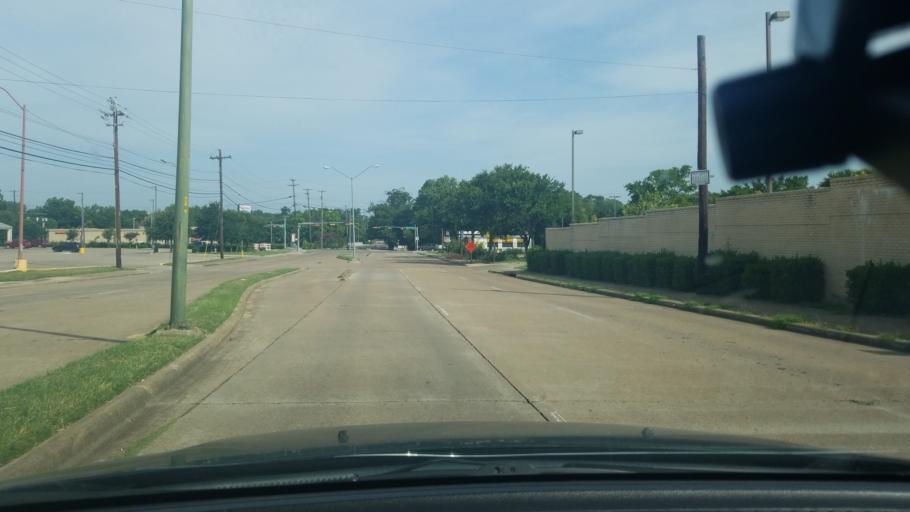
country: US
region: Texas
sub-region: Dallas County
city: Highland Park
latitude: 32.8108
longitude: -96.7000
